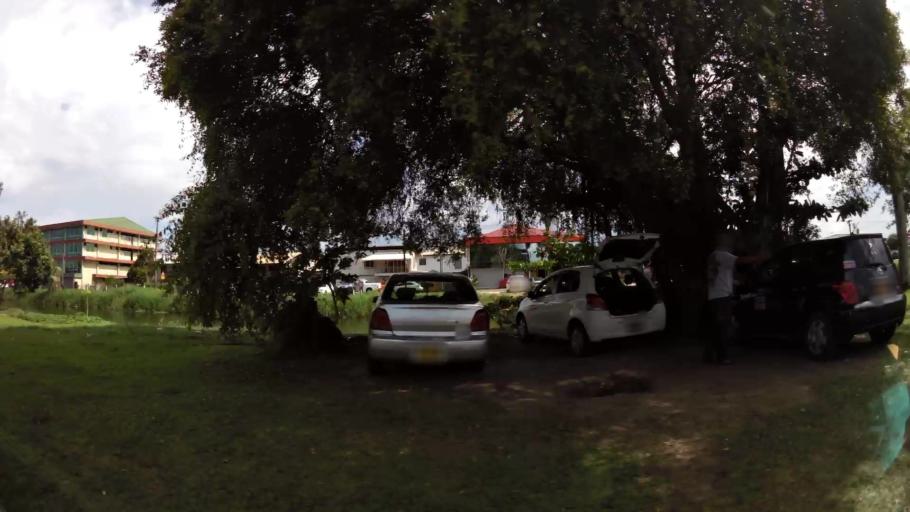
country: SR
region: Paramaribo
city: Paramaribo
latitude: 5.8435
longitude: -55.1444
